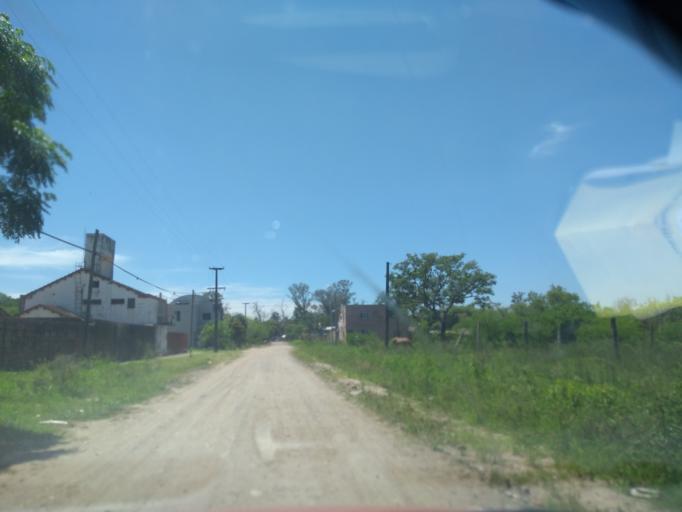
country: AR
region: Chaco
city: Resistencia
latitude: -27.4691
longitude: -58.9603
